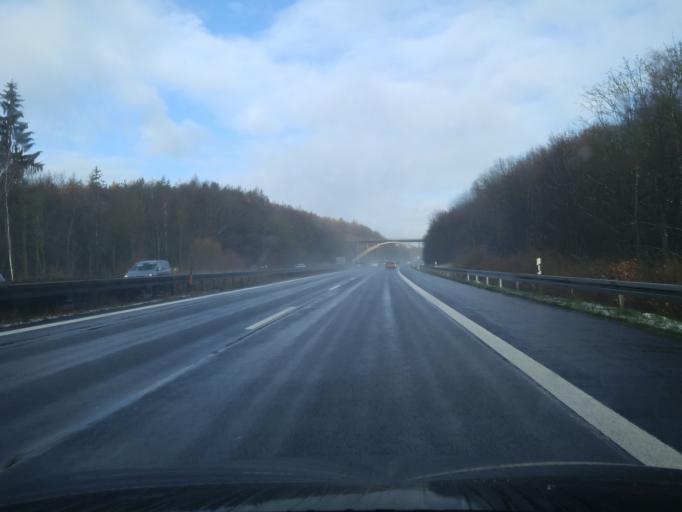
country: DE
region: Bavaria
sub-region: Regierungsbezirk Unterfranken
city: Arnstein
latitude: 49.9202
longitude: 9.9970
